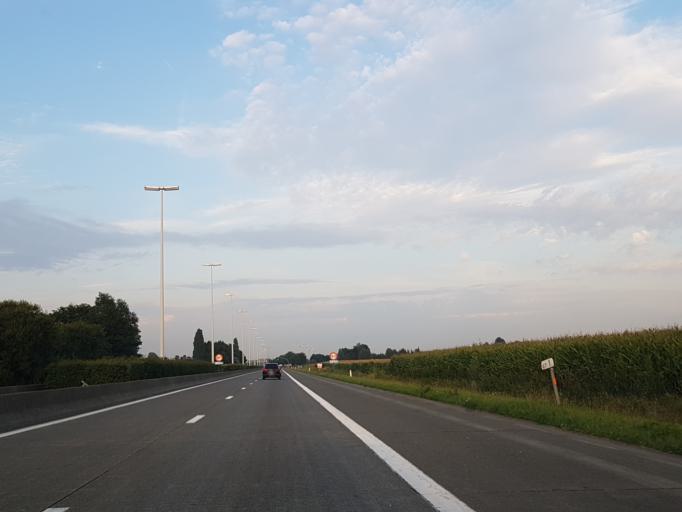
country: BE
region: Flanders
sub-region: Provincie Oost-Vlaanderen
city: Maldegem
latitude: 51.2208
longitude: 3.4226
